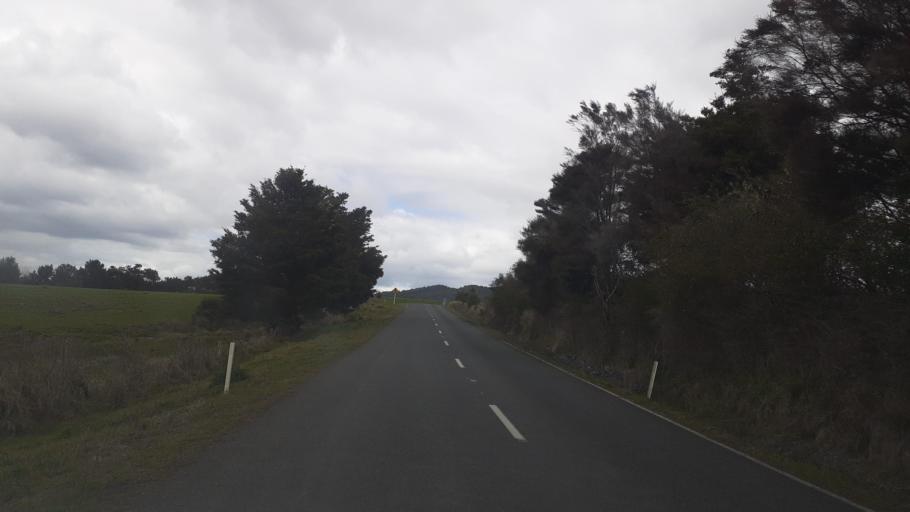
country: NZ
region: Northland
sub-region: Far North District
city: Moerewa
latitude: -35.5893
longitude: 173.9745
